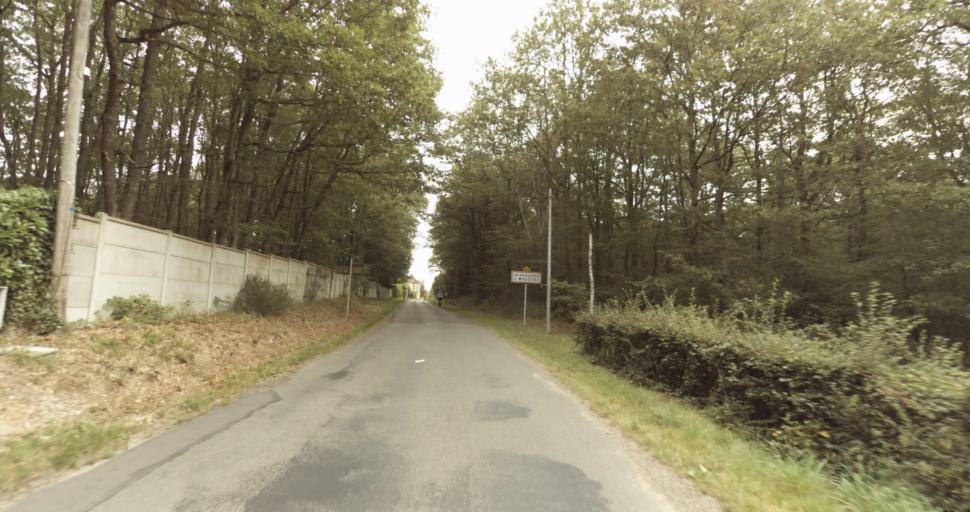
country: FR
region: Haute-Normandie
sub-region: Departement de l'Eure
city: La Couture-Boussey
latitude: 48.8865
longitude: 1.3807
